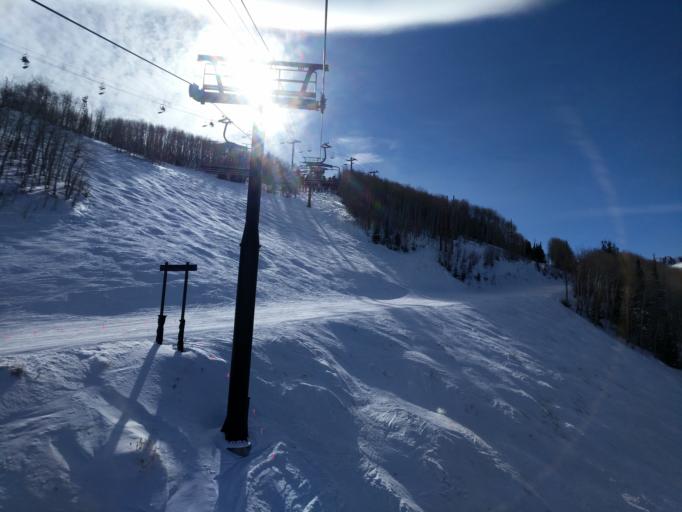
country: US
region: Utah
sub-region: Summit County
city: Park City
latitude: 40.6382
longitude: -111.5082
